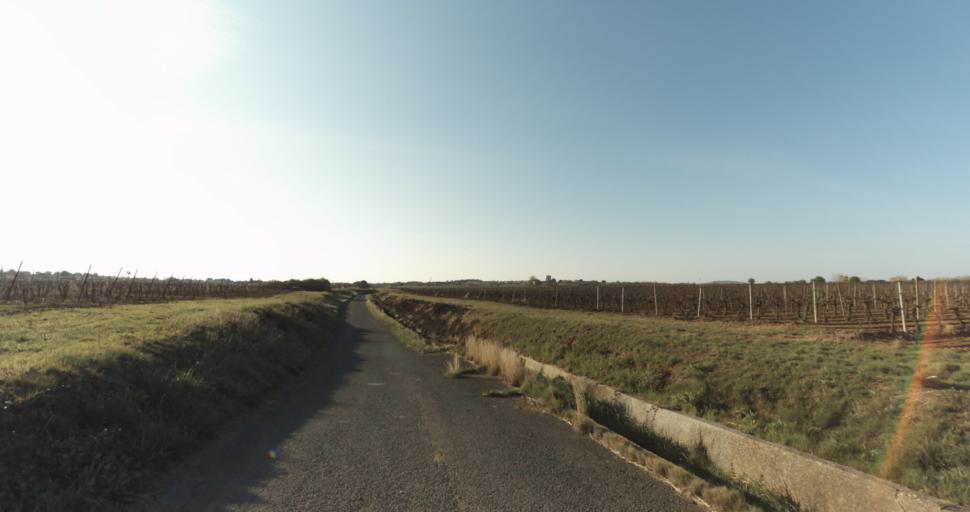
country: FR
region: Languedoc-Roussillon
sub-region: Departement de l'Herault
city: Marseillan
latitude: 43.3764
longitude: 3.5236
